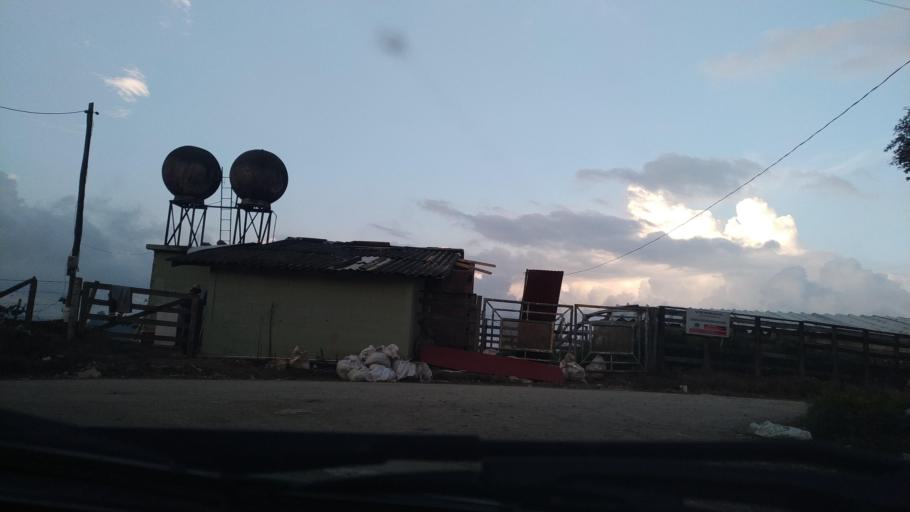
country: CO
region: Antioquia
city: Marinilla
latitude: 6.1934
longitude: -75.2828
